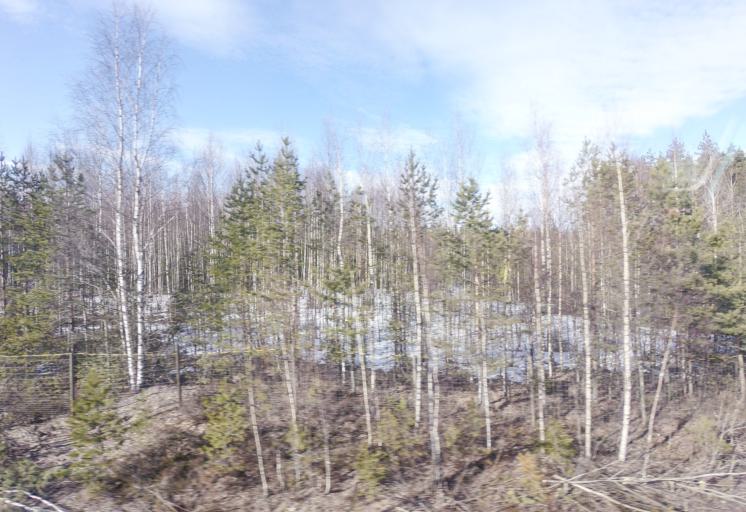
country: FI
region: South Karelia
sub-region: Lappeenranta
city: Joutseno
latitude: 61.0986
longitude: 28.3872
